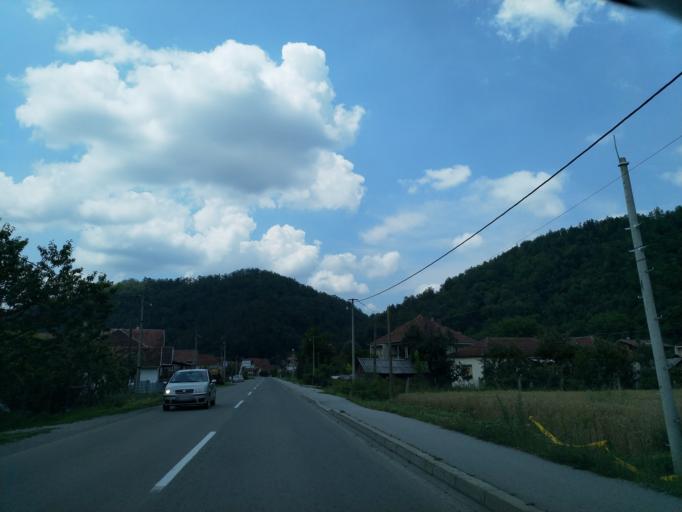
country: RS
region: Central Serbia
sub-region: Rasinski Okrug
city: Aleksandrovac
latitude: 43.3732
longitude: 21.0512
